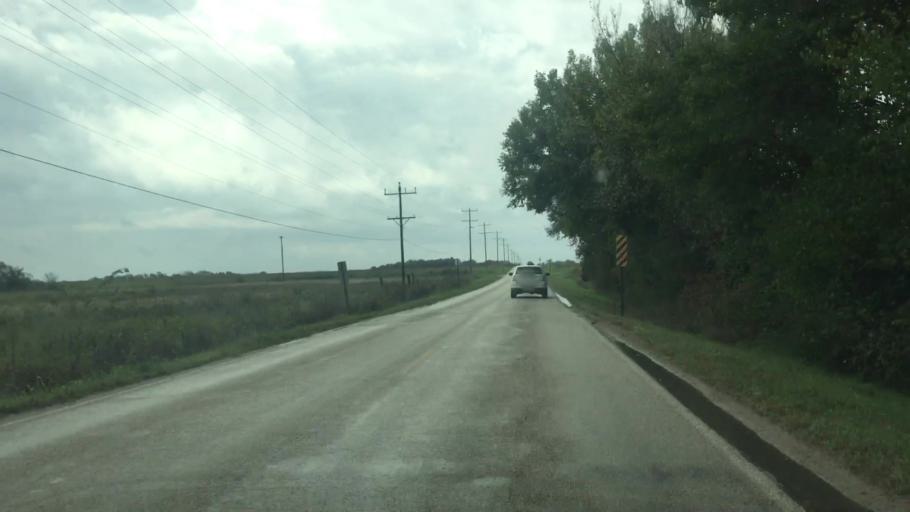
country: US
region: Kansas
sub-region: Allen County
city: Humboldt
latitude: 37.8508
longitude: -95.4369
